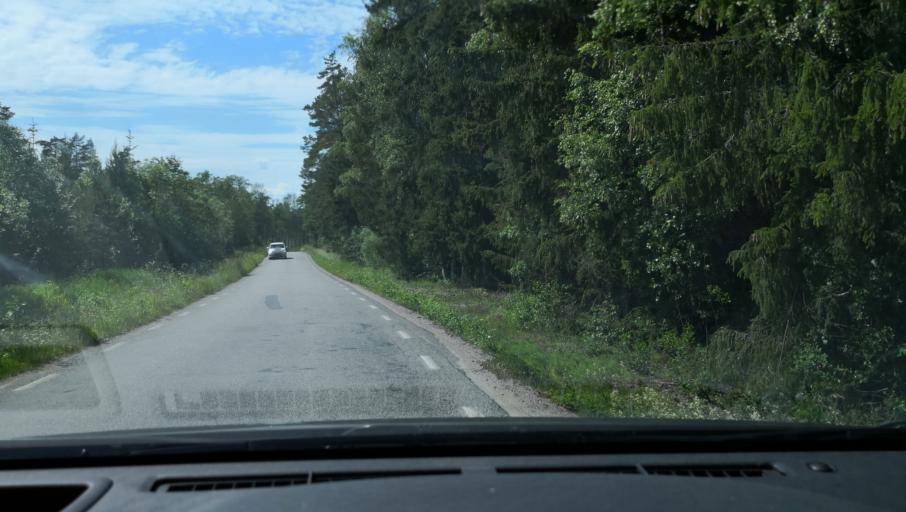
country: SE
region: Stockholm
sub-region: Sigtuna Kommun
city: Sigtuna
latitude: 59.6896
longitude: 17.6640
